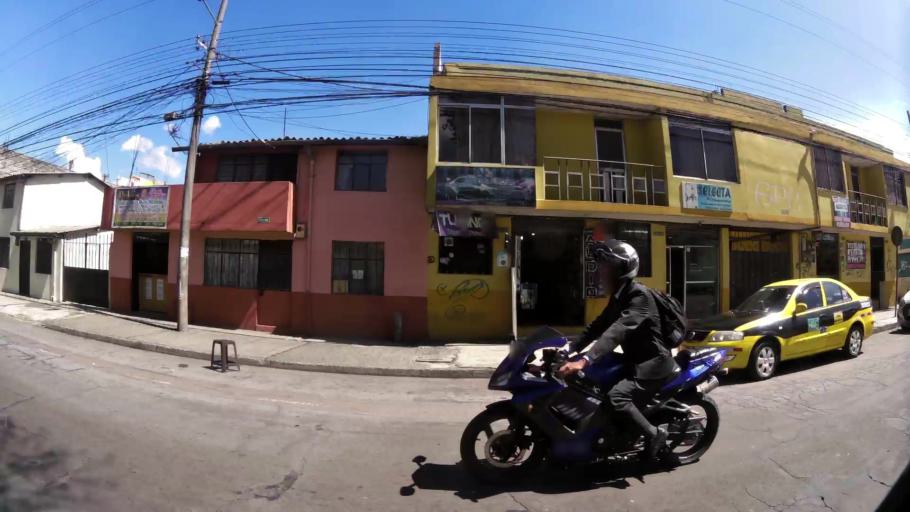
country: EC
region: Pichincha
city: Quito
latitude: -0.2573
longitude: -78.5334
